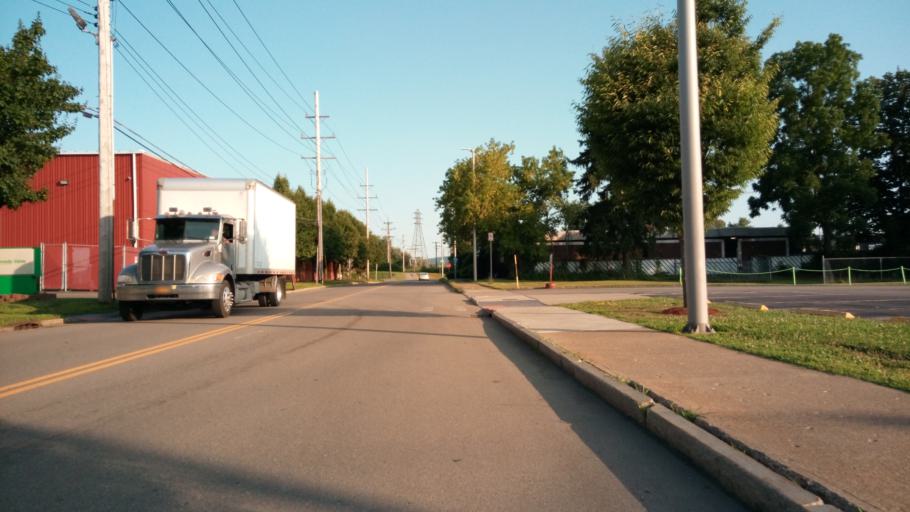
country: US
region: New York
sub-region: Chemung County
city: Elmira
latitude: 42.0910
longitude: -76.7895
